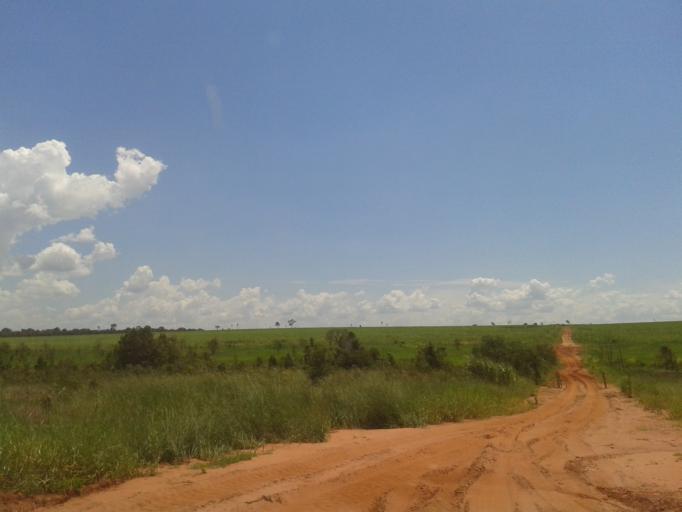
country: BR
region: Minas Gerais
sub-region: Santa Vitoria
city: Santa Vitoria
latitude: -19.1728
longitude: -50.4343
